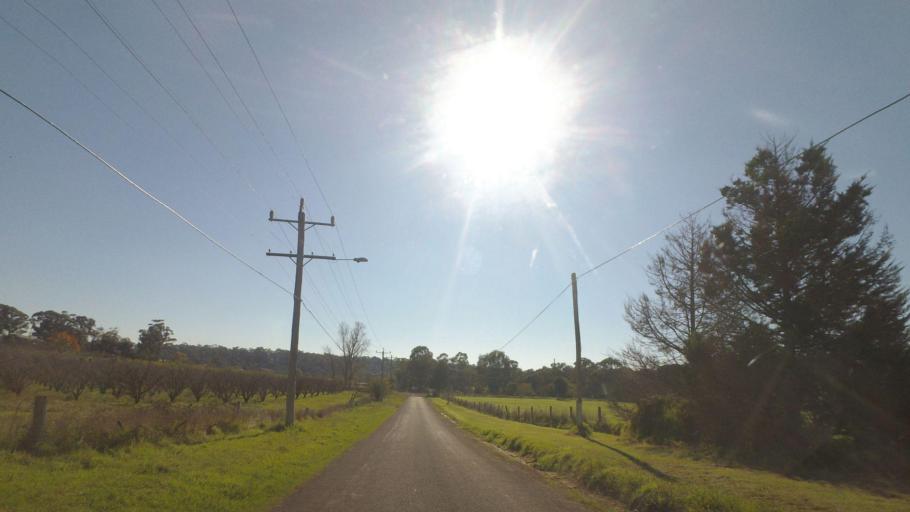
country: AU
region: Victoria
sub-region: Nillumbik
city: Eltham
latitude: -37.7410
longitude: 145.1556
